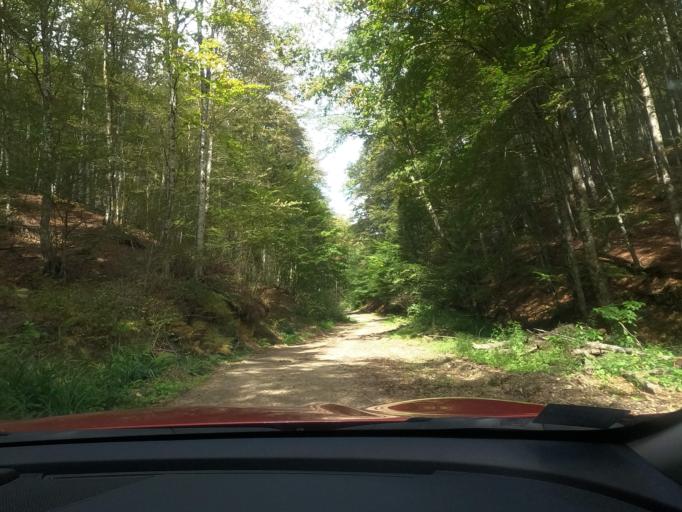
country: BA
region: Federation of Bosnia and Herzegovina
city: Velika Kladusa
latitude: 45.2412
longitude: 15.7739
